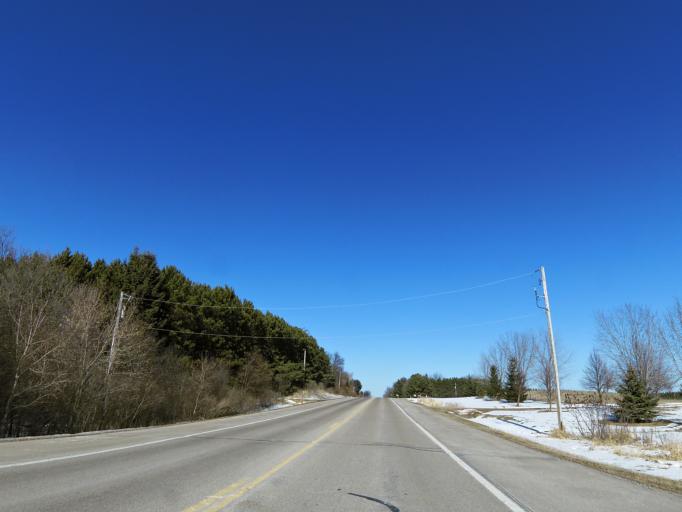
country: US
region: Minnesota
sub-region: Washington County
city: Lake Elmo
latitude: 45.0245
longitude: -92.8833
